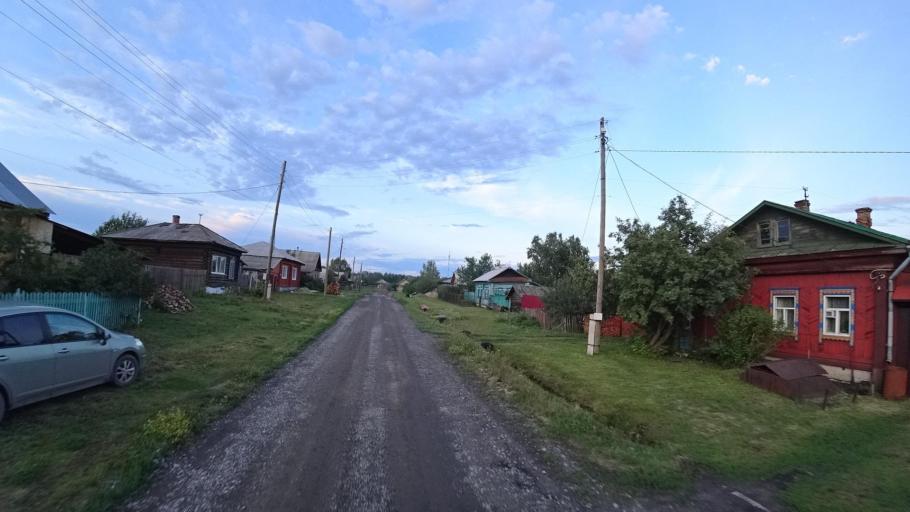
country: RU
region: Sverdlovsk
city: Kamyshlov
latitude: 56.8578
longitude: 62.7121
